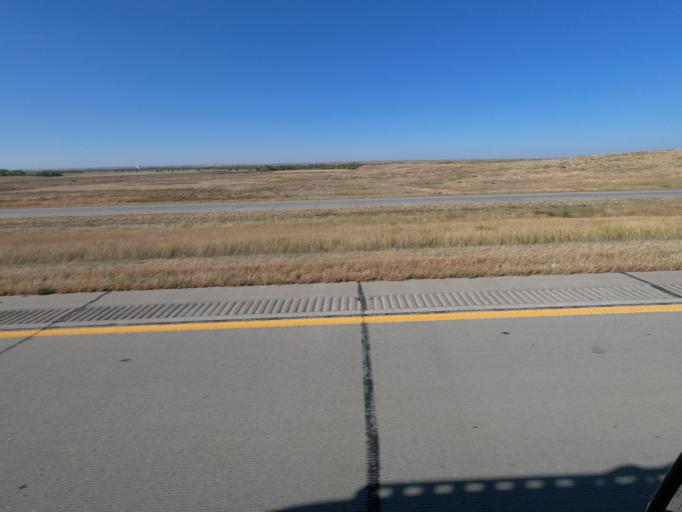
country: US
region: Colorado
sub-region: Sedgwick County
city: Julesburg
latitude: 40.9281
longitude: -102.3338
